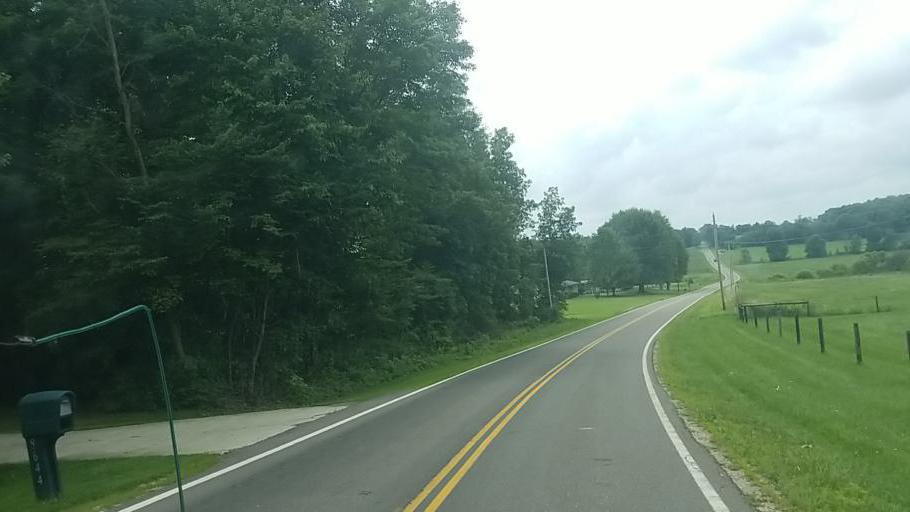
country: US
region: Ohio
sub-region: Licking County
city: Utica
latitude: 40.2193
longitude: -82.3799
